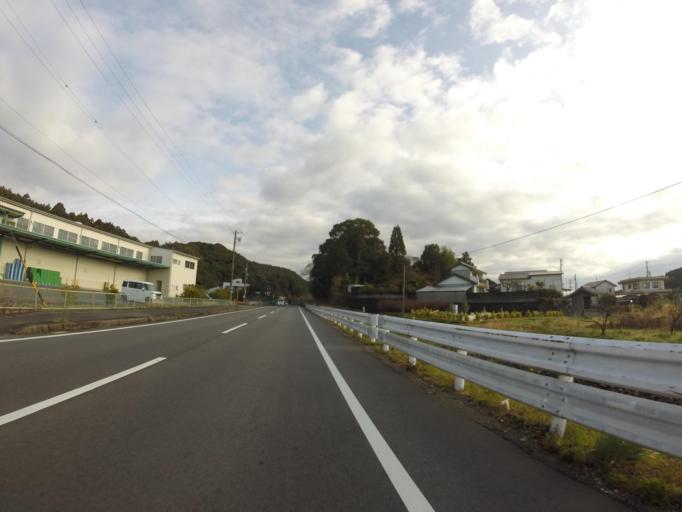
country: JP
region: Shizuoka
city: Hamakita
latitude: 34.8227
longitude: 137.7142
